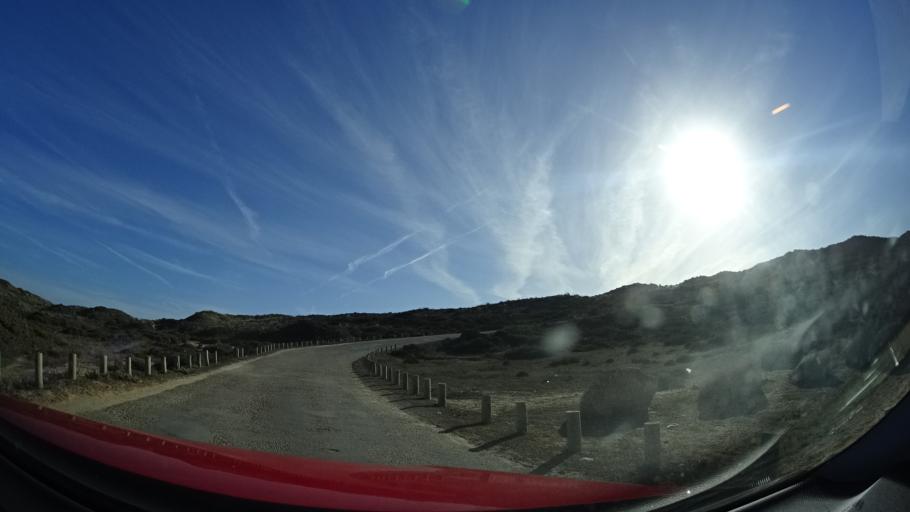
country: PT
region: Faro
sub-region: Vila do Bispo
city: Vila do Bispo
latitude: 37.1925
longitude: -8.9024
